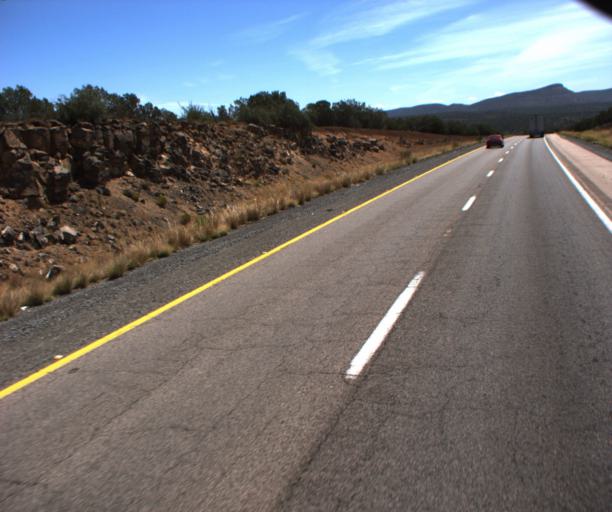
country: US
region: Arizona
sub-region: Mohave County
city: Peach Springs
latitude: 35.1900
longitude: -113.3284
